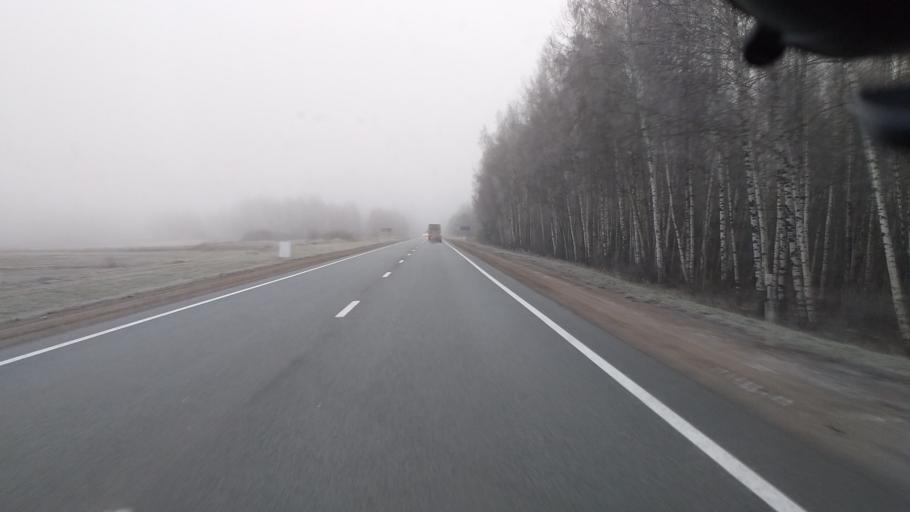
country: LV
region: Marupe
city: Marupe
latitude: 56.8505
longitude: 24.0074
